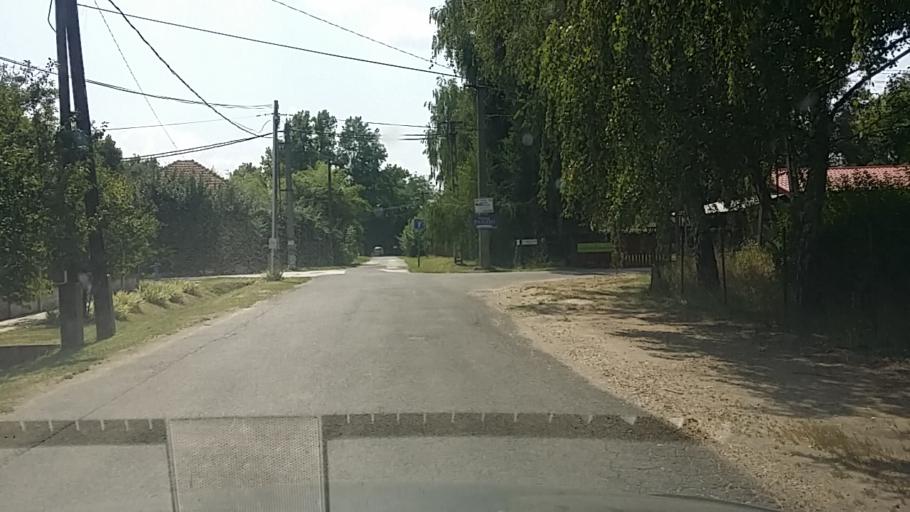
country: HU
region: Bekes
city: Gyomaendrod
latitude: 46.9360
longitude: 20.8387
